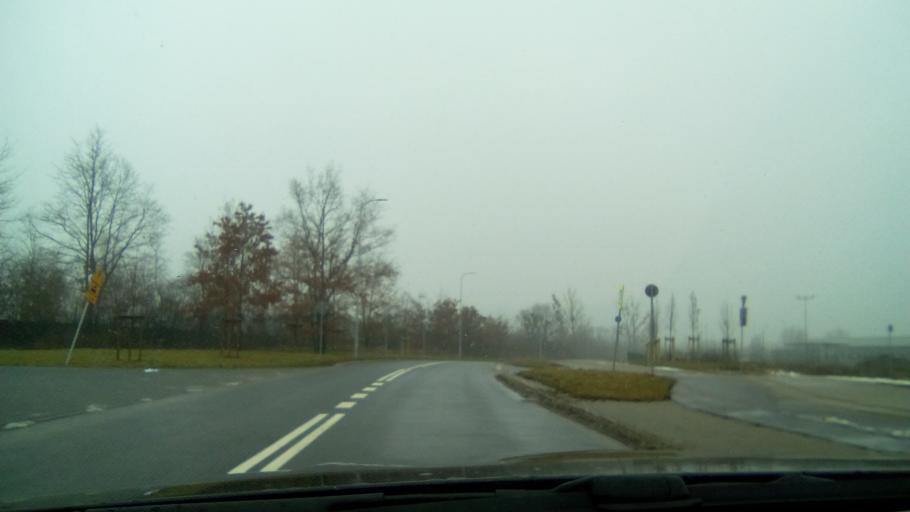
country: PL
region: Greater Poland Voivodeship
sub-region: Powiat poznanski
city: Swarzedz
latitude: 52.3876
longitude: 17.0095
